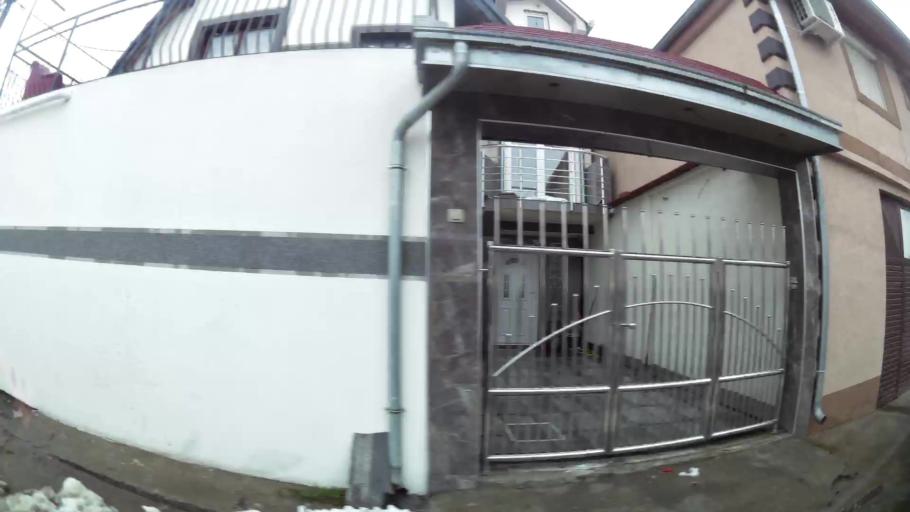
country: RS
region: Central Serbia
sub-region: Belgrade
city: Zemun
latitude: 44.8434
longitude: 20.3716
